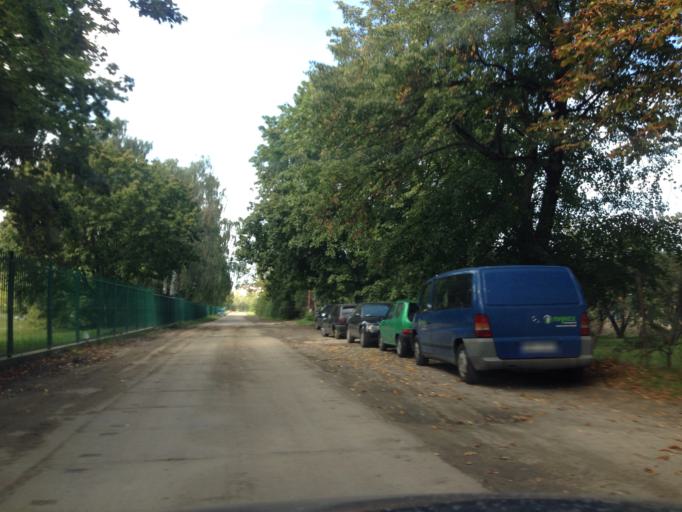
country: PL
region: Pomeranian Voivodeship
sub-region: Gdansk
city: Gdansk
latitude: 54.3974
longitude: 18.6175
